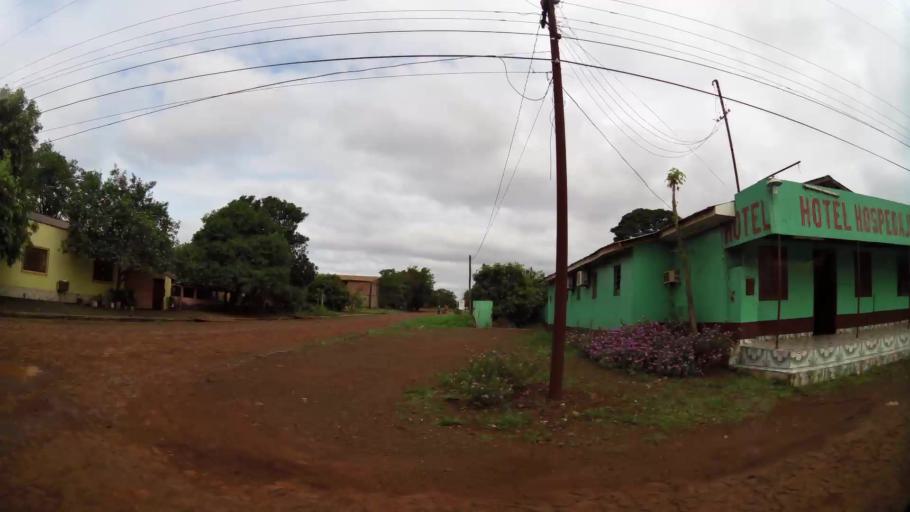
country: PY
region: Alto Parana
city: Ciudad del Este
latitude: -25.3885
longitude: -54.6434
